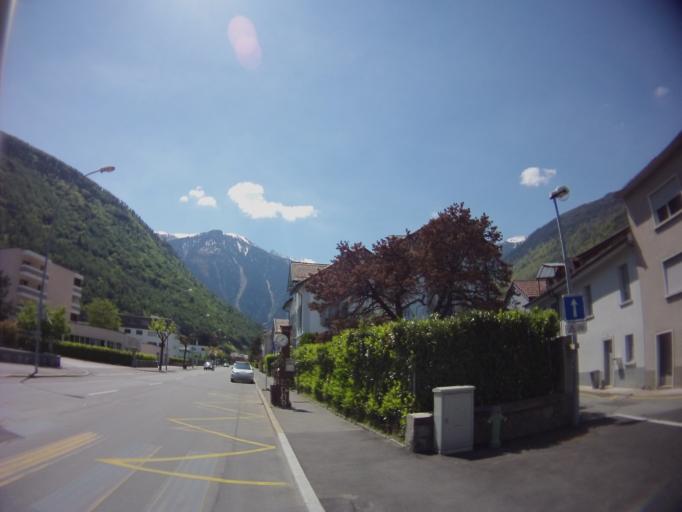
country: CH
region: Valais
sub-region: Martigny District
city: Martigny-Ville
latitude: 46.0958
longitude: 7.0680
